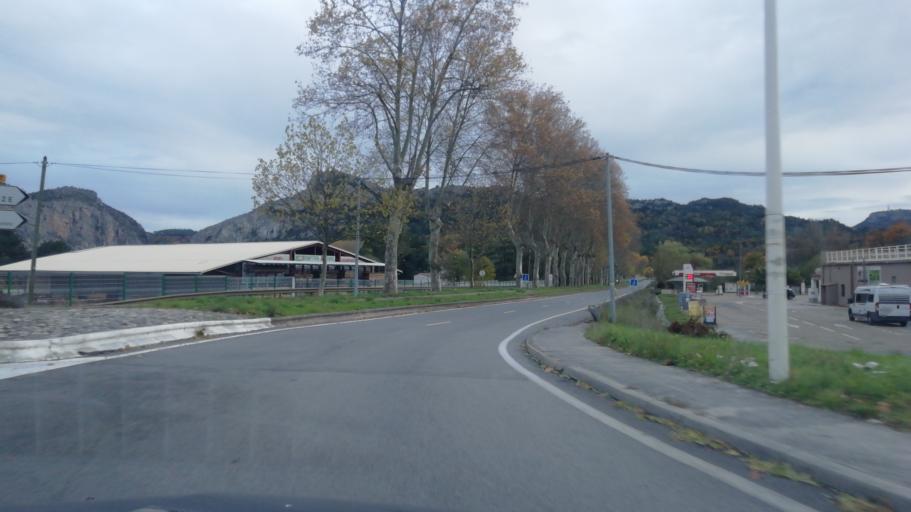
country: FR
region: Languedoc-Roussillon
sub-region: Departement du Gard
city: Anduze
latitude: 44.0658
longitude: 3.9710
